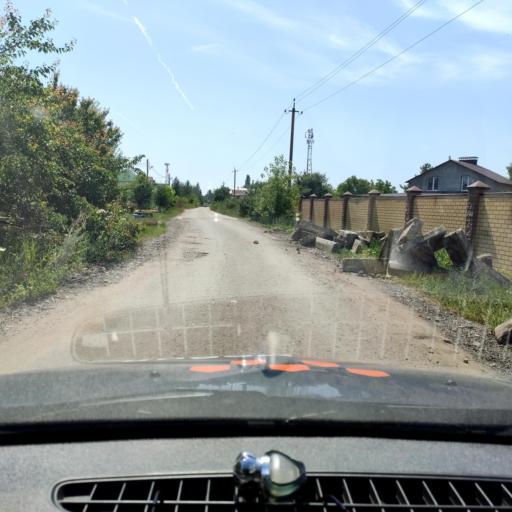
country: RU
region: Voronezj
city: Ramon'
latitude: 51.8325
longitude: 39.2649
